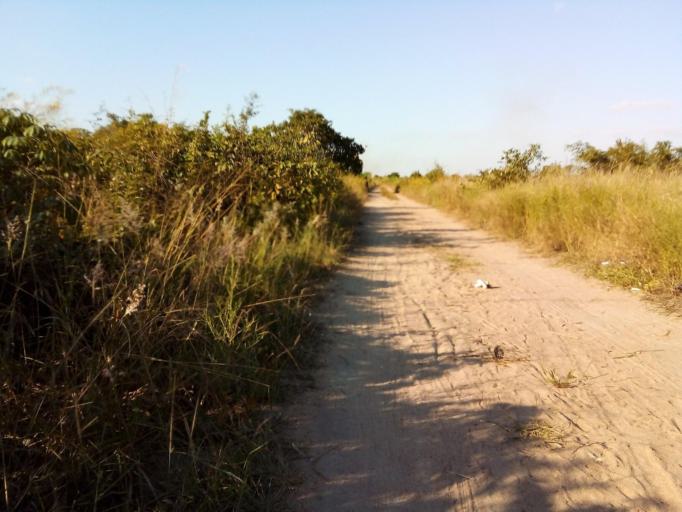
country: MZ
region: Zambezia
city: Quelimane
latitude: -17.5511
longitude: 36.7061
